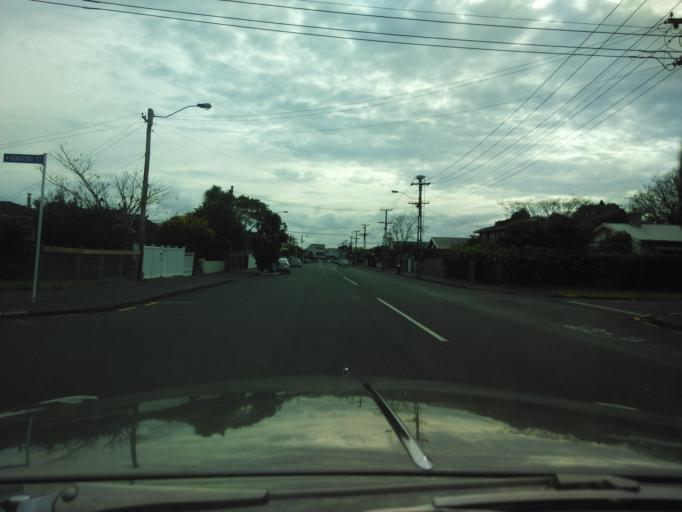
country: NZ
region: Auckland
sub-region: Auckland
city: Rosebank
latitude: -36.8622
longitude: 174.7040
